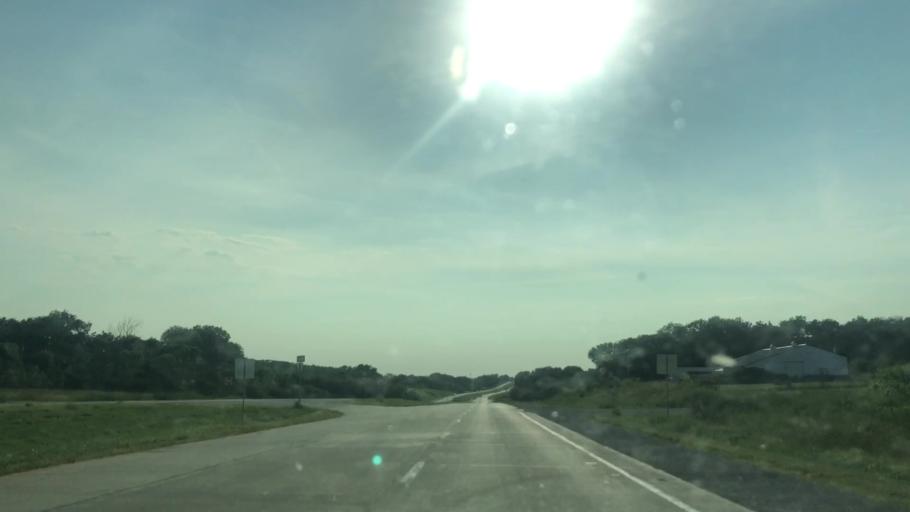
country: US
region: Iowa
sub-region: Story County
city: Nevada
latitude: 42.0079
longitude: -93.3695
